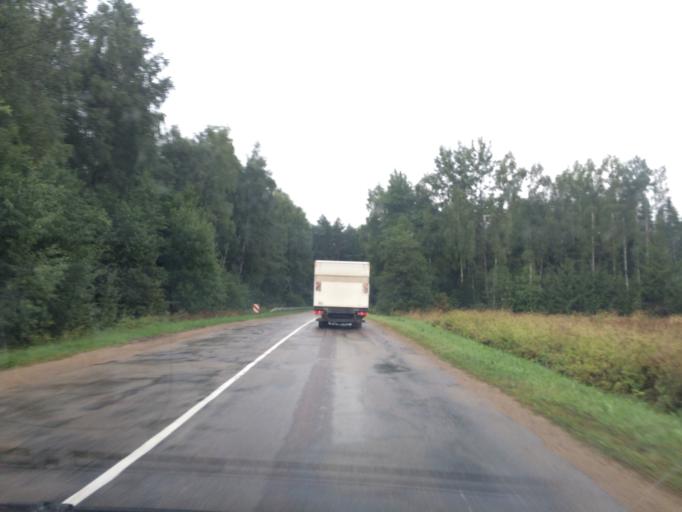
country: LV
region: Ikskile
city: Ikskile
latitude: 56.8559
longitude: 24.5377
